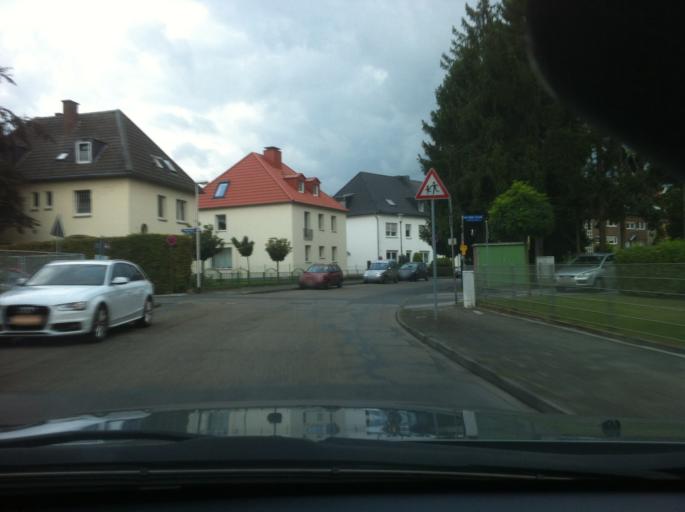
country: DE
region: North Rhine-Westphalia
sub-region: Regierungsbezirk Dusseldorf
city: Kleve
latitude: 51.7835
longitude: 6.1366
